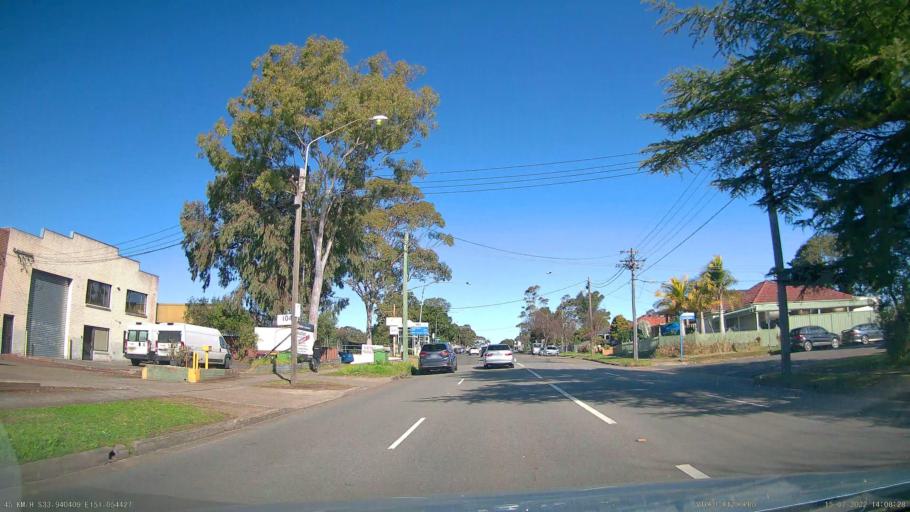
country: AU
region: New South Wales
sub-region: Canterbury
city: Roselands
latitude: -33.9406
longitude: 151.0544
